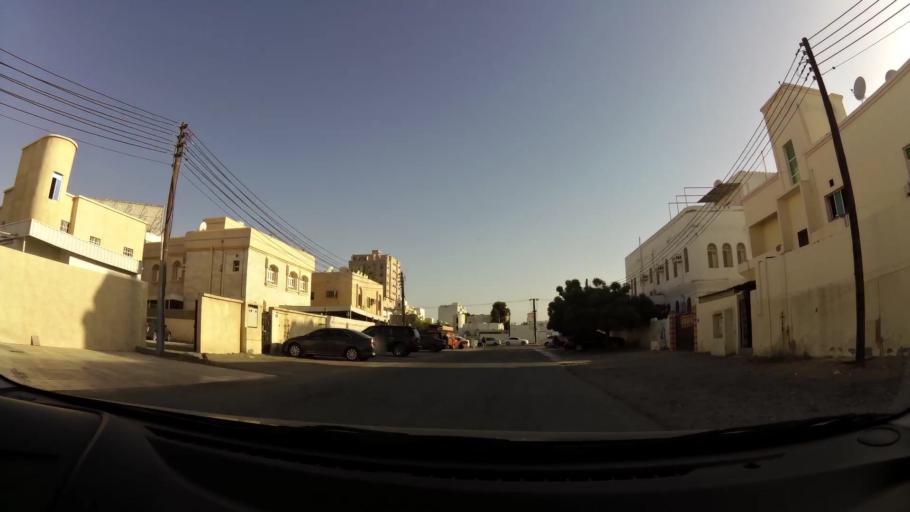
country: OM
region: Muhafazat Masqat
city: As Sib al Jadidah
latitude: 23.6305
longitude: 58.1965
